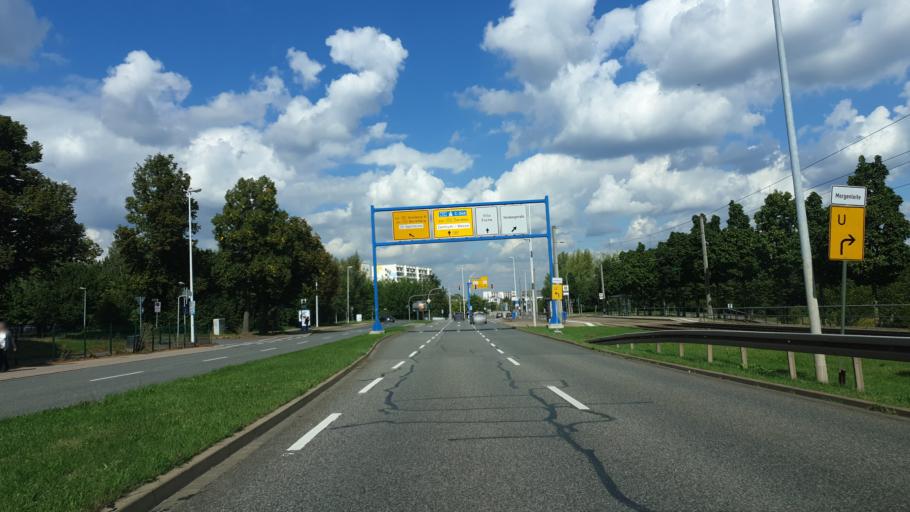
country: DE
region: Saxony
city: Neukirchen
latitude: 50.8001
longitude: 12.8838
